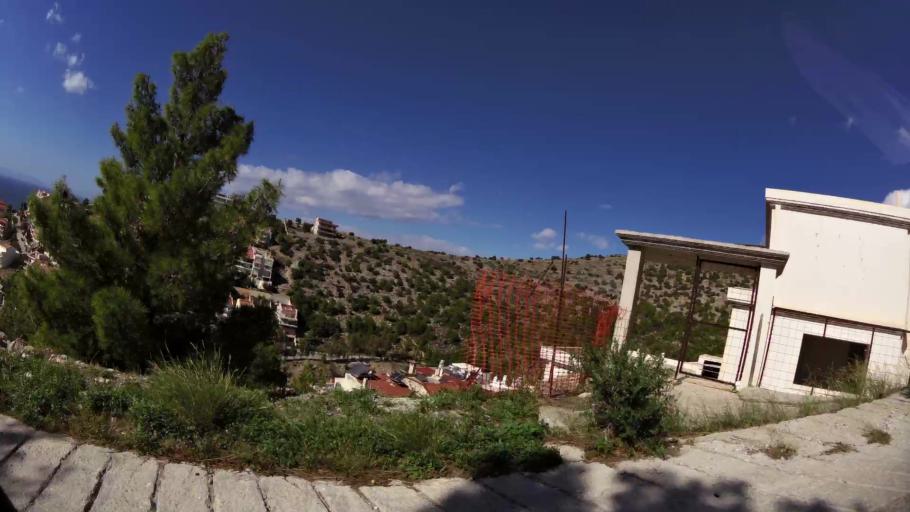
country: GR
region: Attica
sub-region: Nomarchia Anatolikis Attikis
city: Voula
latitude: 37.8599
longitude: 23.7828
